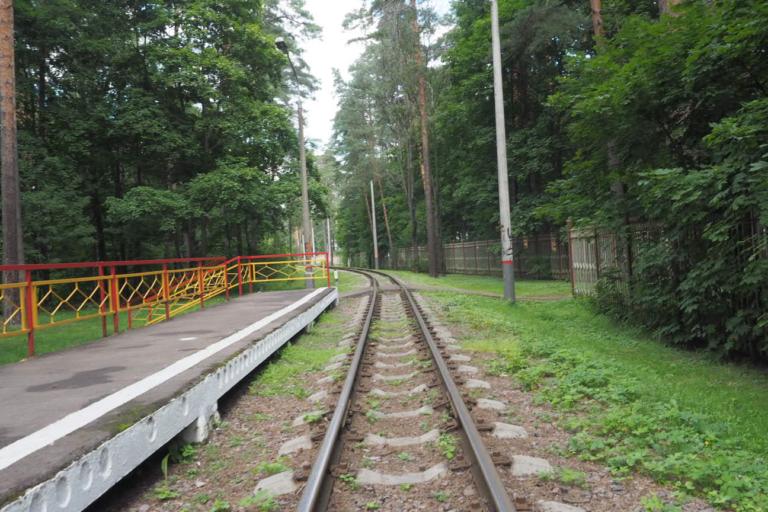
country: RU
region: Moskovskaya
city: Zhukovskiy
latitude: 55.5956
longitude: 38.1432
